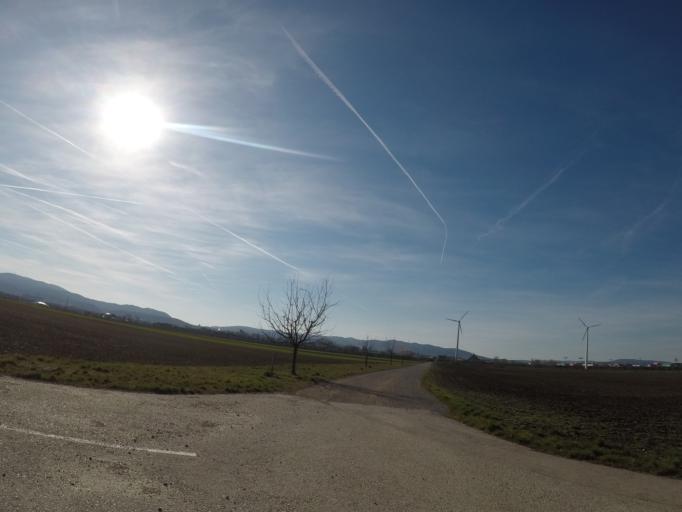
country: AT
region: Lower Austria
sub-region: Politischer Bezirk Modling
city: Vosendorf
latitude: 48.1081
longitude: 16.3324
